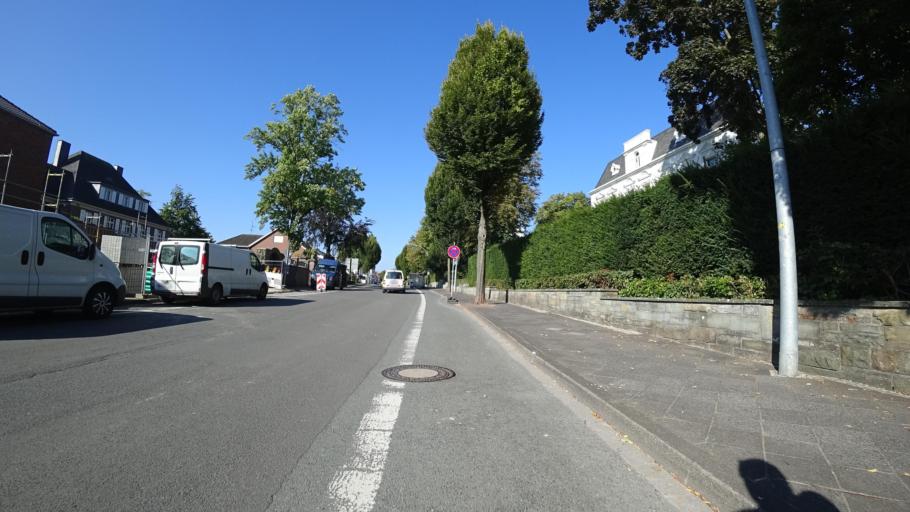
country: DE
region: North Rhine-Westphalia
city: Oelde
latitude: 51.8257
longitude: 8.1402
